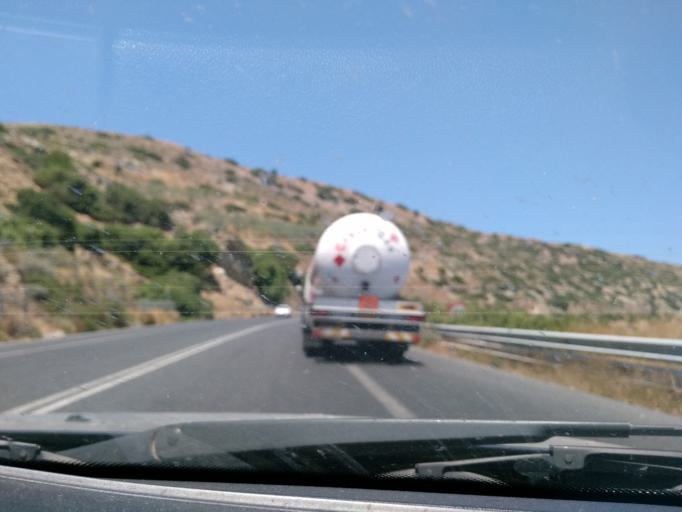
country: GR
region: Crete
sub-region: Nomos Irakleiou
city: Gazi
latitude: 35.3777
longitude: 25.0360
